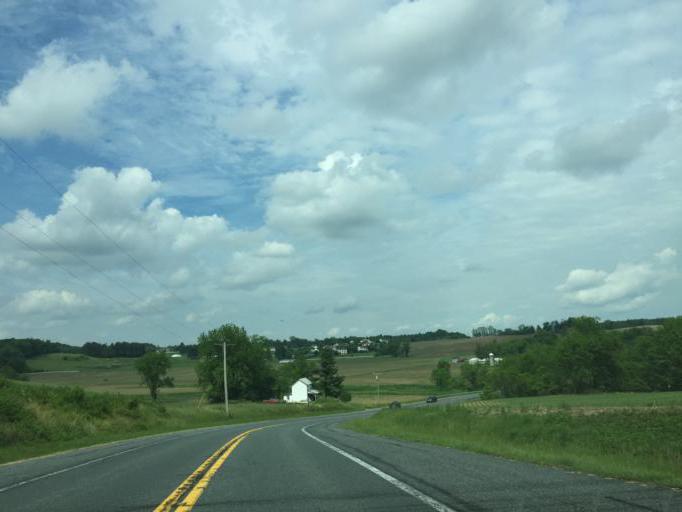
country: US
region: Maryland
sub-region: Harford County
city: Jarrettsville
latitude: 39.6649
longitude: -76.4448
